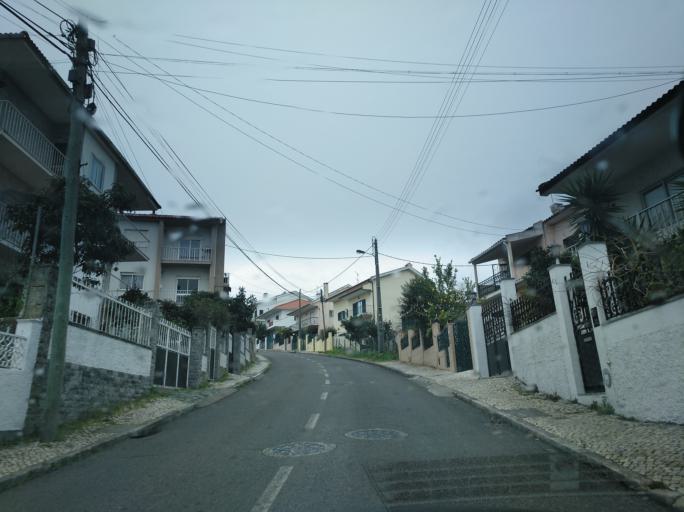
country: PT
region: Lisbon
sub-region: Odivelas
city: Famoes
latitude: 38.7939
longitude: -9.2112
